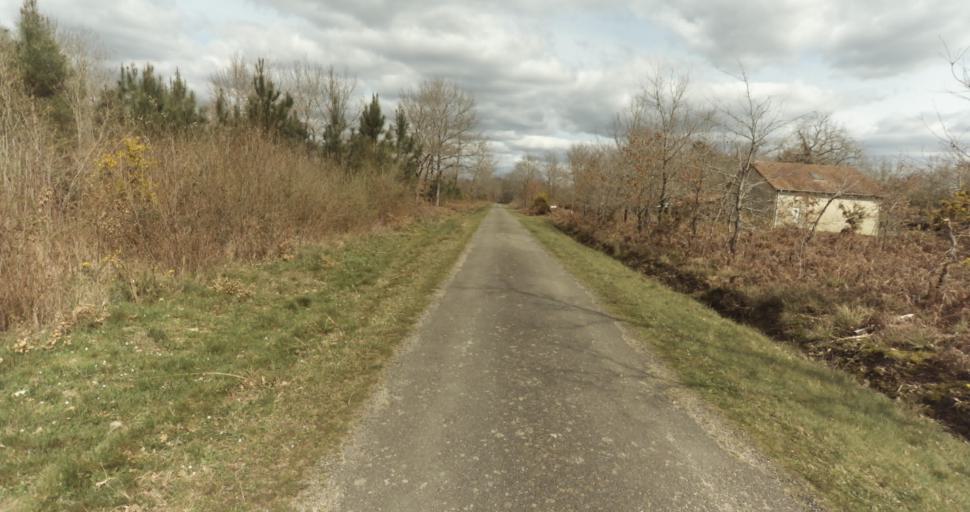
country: FR
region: Aquitaine
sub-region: Departement des Landes
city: Roquefort
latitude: 44.0694
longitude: -0.4152
